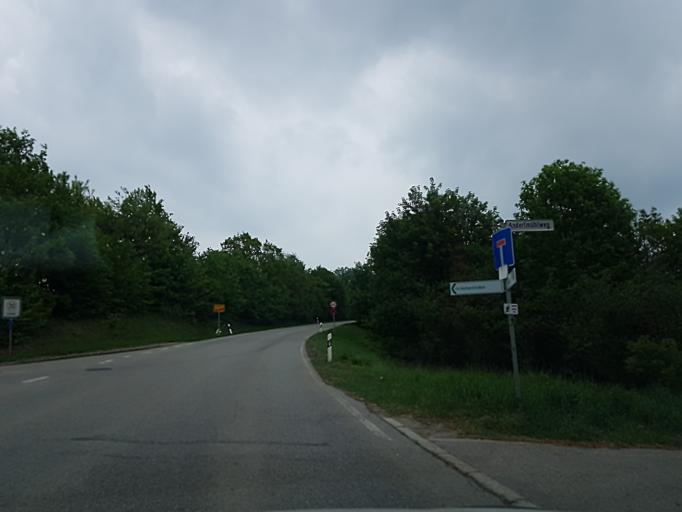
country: DE
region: Bavaria
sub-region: Upper Bavaria
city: Ebersberg
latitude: 48.0870
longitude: 11.9694
